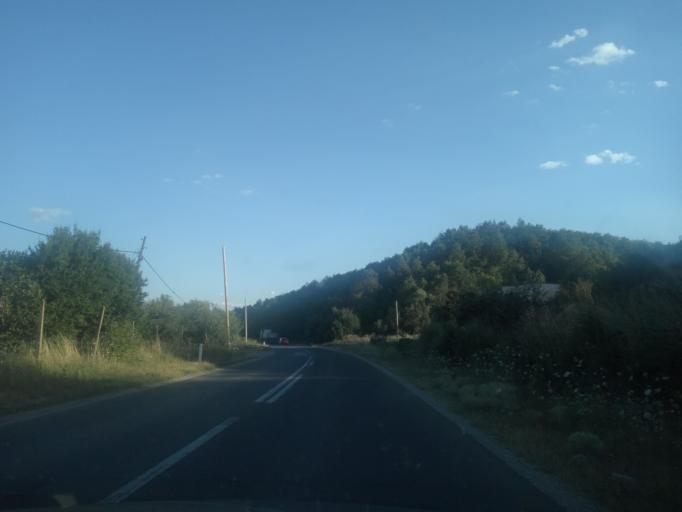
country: XK
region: Pec
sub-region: Komuna e Pejes
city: Kosuriq
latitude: 42.4680
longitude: 20.5045
